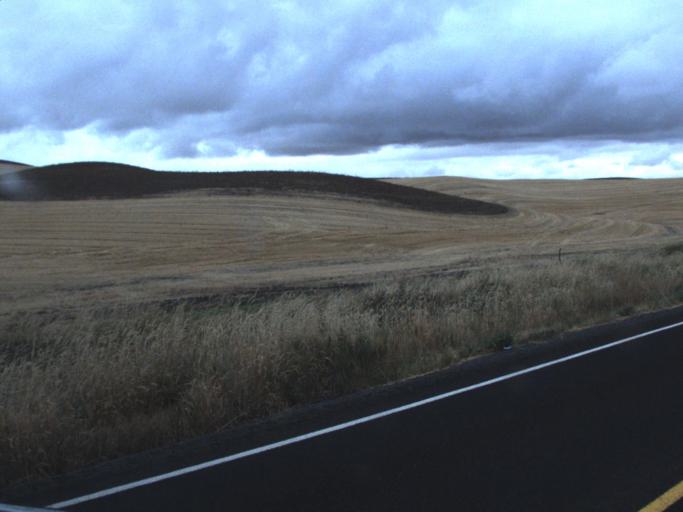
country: US
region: Washington
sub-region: Whitman County
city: Colfax
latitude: 47.1718
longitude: -117.2914
